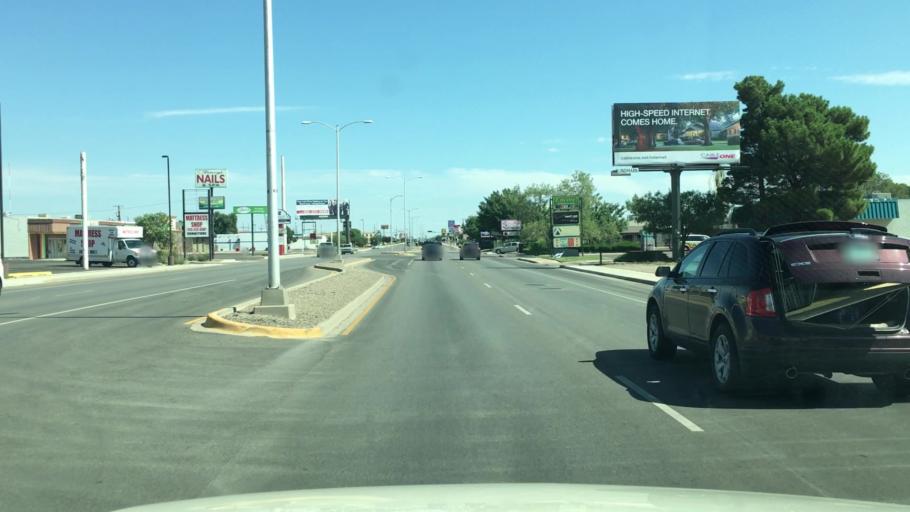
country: US
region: New Mexico
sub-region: Chaves County
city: Roswell
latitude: 33.4343
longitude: -104.5231
